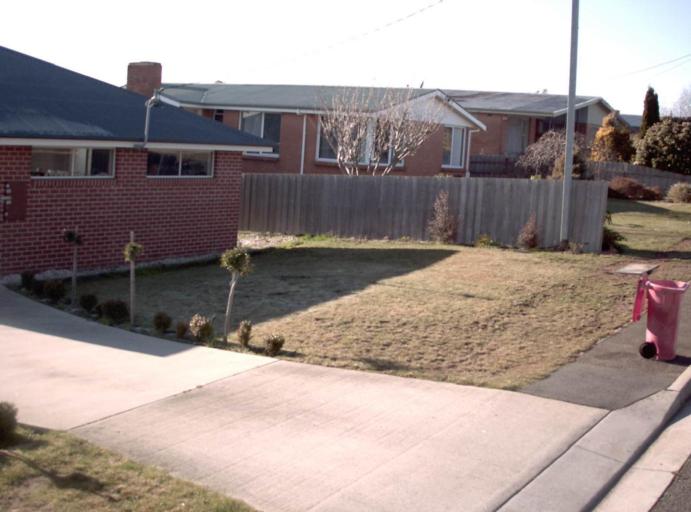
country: AU
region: Tasmania
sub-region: Launceston
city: Summerhill
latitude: -41.4675
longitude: 147.1232
